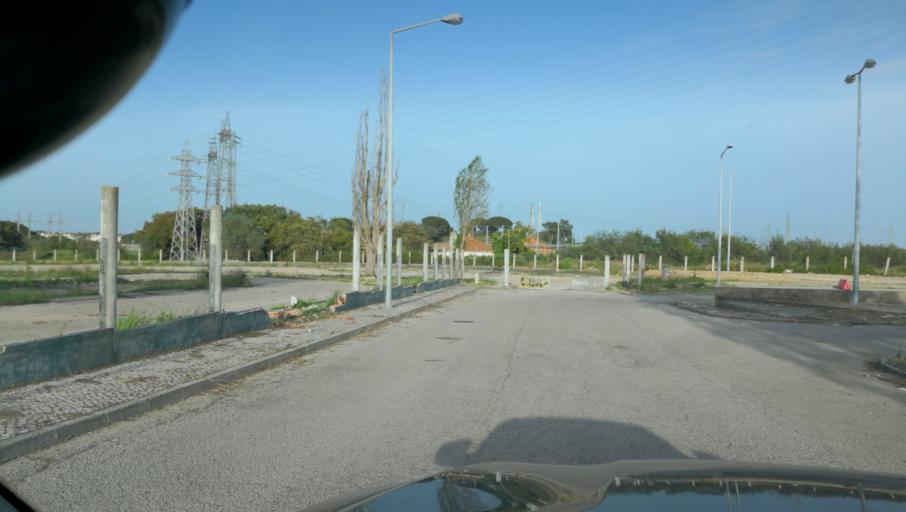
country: PT
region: Setubal
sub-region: Setubal
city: Setubal
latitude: 38.5371
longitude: -8.8647
